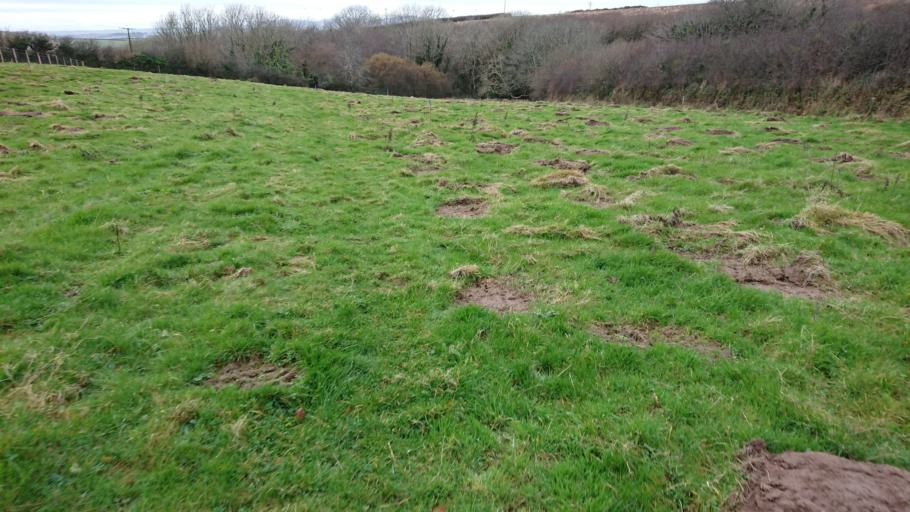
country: GB
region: England
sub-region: Cornwall
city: Fowey
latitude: 50.3396
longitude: -4.5681
